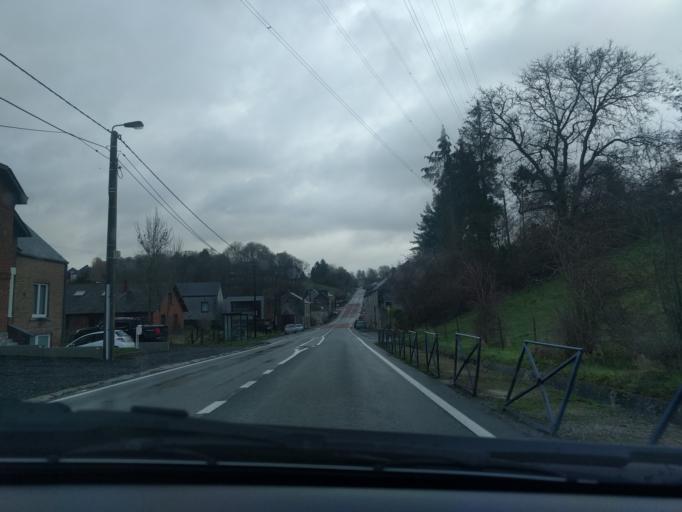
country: BE
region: Wallonia
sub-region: Province de Namur
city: Noville-les-Bois
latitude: 50.5053
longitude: 4.9526
